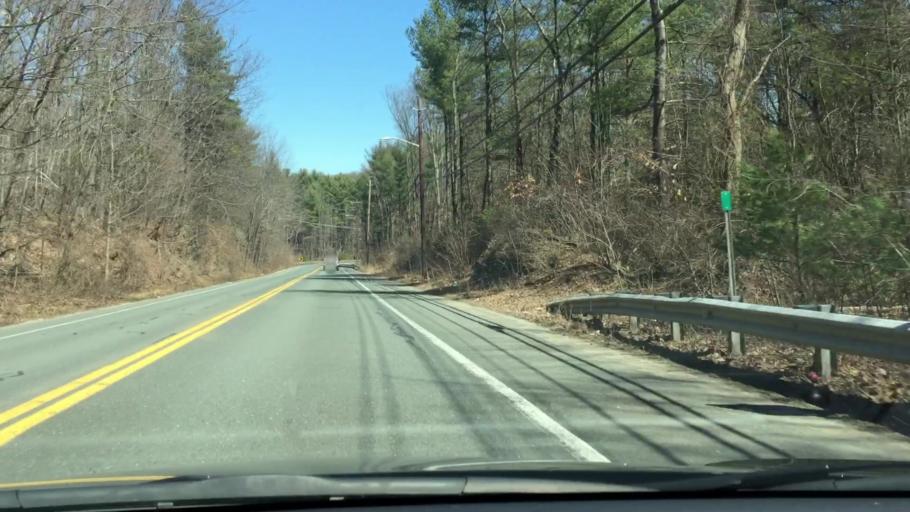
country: US
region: Massachusetts
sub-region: Hampden County
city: Holyoke
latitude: 42.1846
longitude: -72.6617
